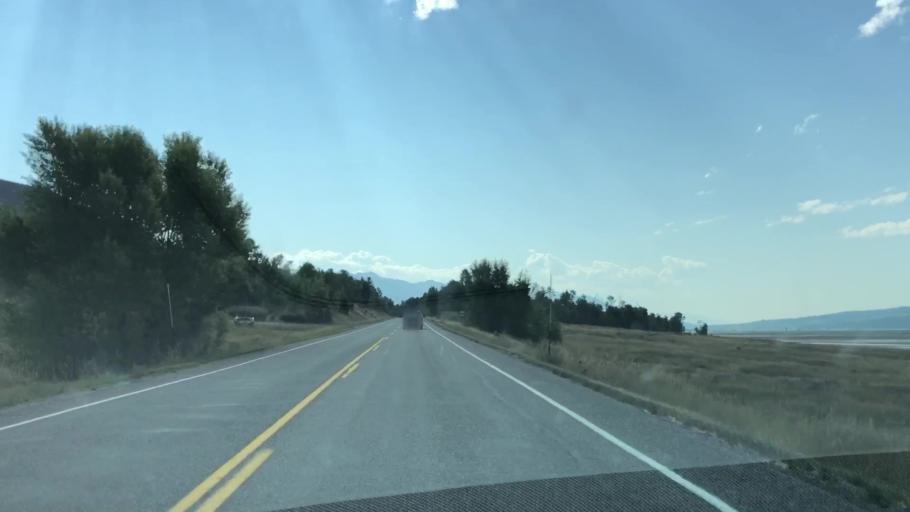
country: US
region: Wyoming
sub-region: Teton County
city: Hoback
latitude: 43.2137
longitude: -111.0616
